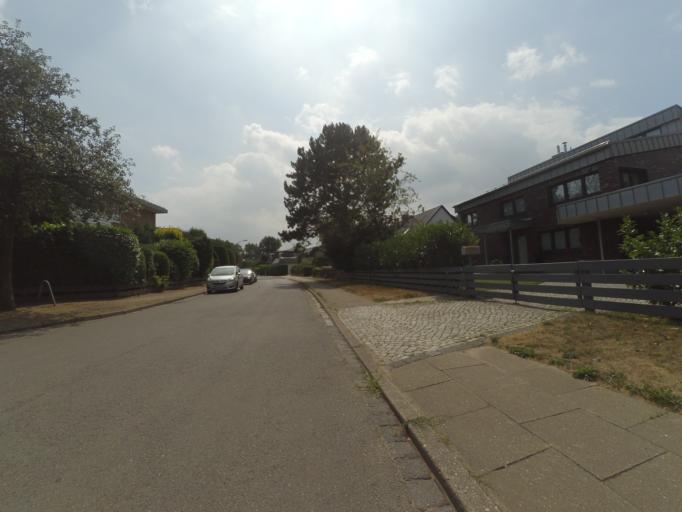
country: DE
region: Schleswig-Holstein
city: Bonningstedt
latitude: 53.6336
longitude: 9.9369
